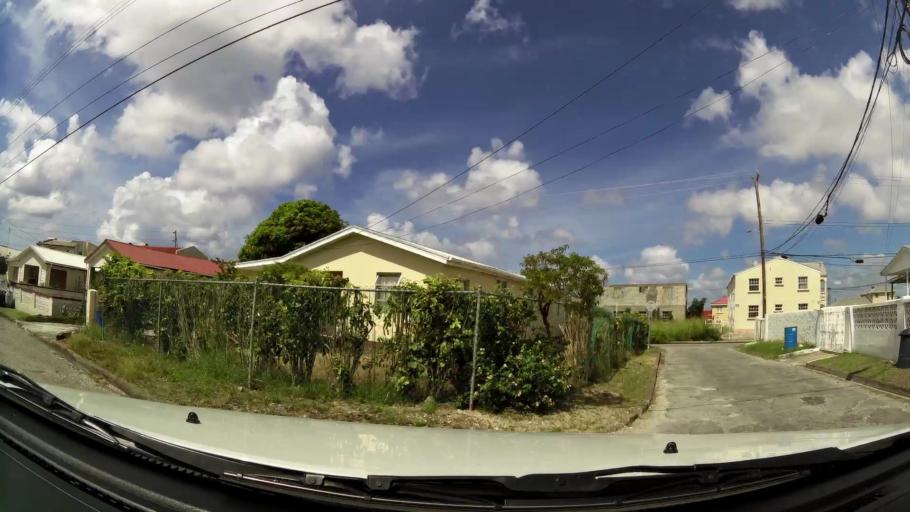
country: BB
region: Saint James
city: Holetown
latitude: 13.1515
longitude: -59.6292
